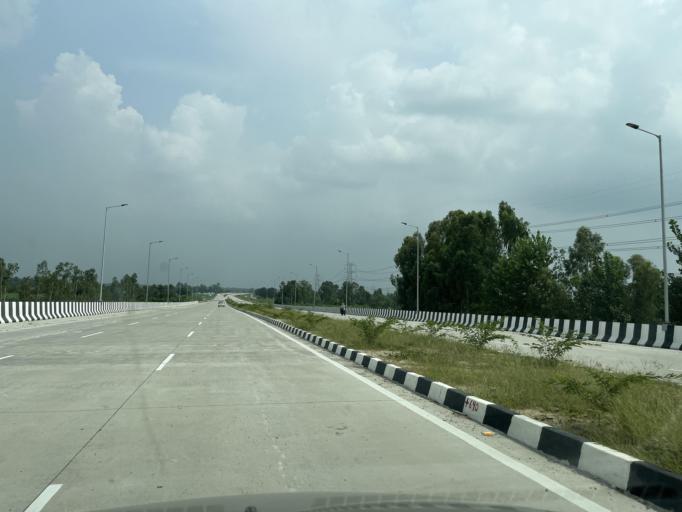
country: IN
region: Uttarakhand
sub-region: Udham Singh Nagar
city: Jaspur
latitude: 29.2940
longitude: 78.8443
